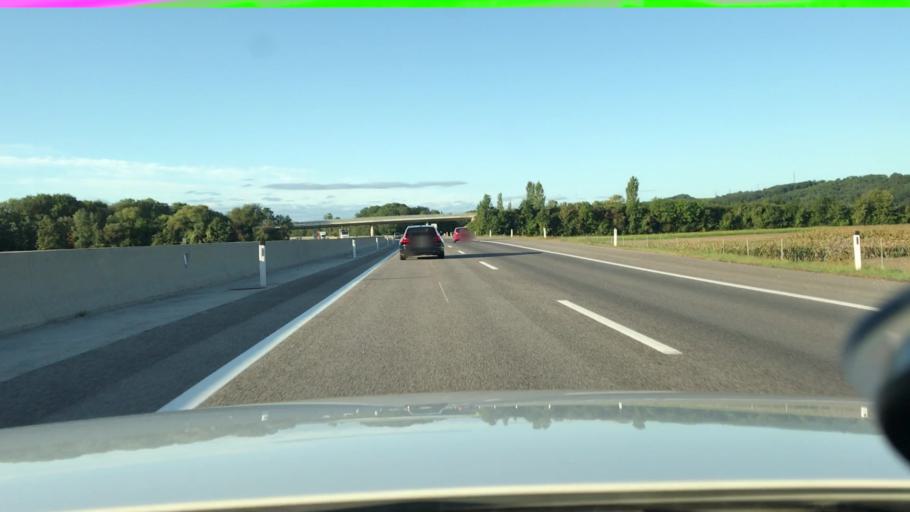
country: AT
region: Lower Austria
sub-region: Politischer Bezirk Sankt Polten
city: Herzogenburg
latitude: 48.2498
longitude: 15.6880
